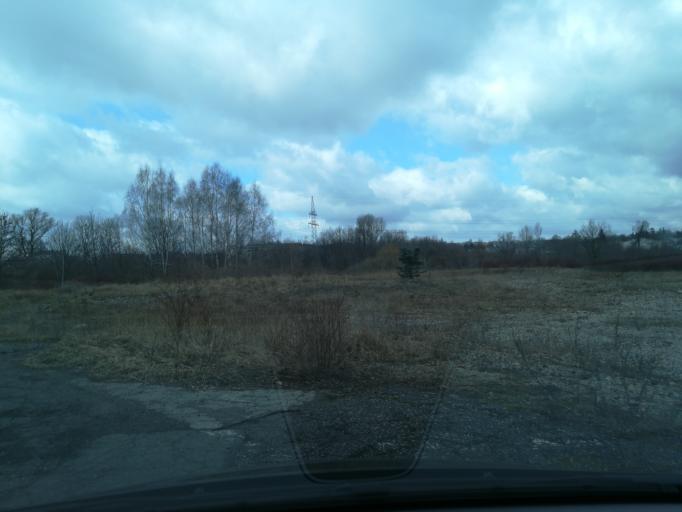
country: PL
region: Silesian Voivodeship
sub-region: Czestochowa
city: Czestochowa
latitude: 50.8221
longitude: 19.1387
